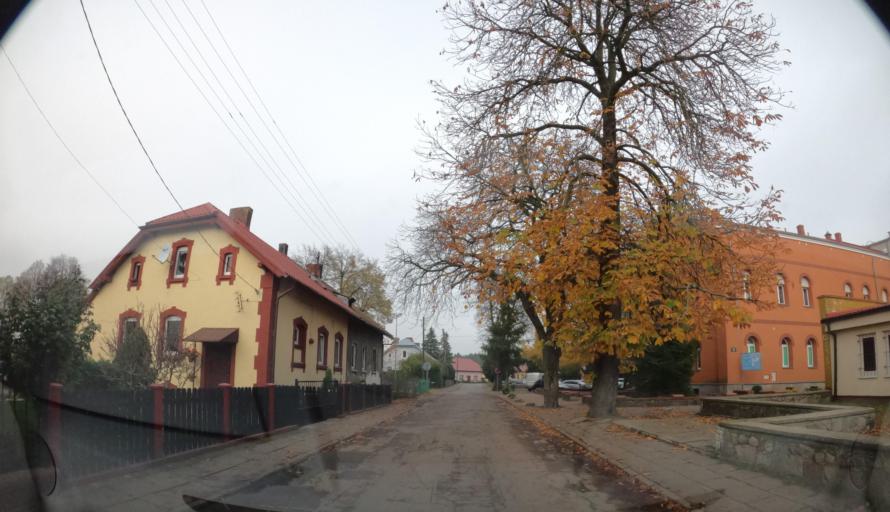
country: PL
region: West Pomeranian Voivodeship
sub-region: Powiat goleniowski
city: Goleniow
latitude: 53.5744
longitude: 14.8349
